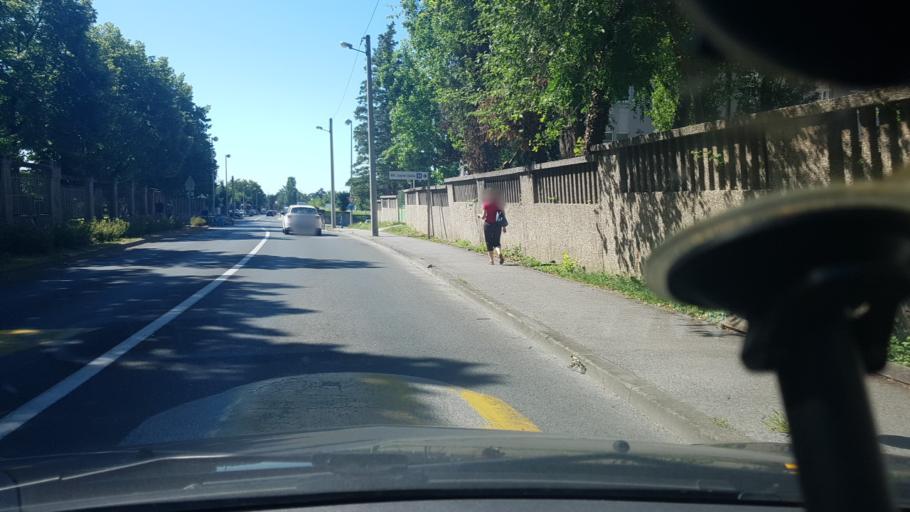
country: HR
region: Grad Zagreb
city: Zagreb
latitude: 45.8217
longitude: 15.9861
